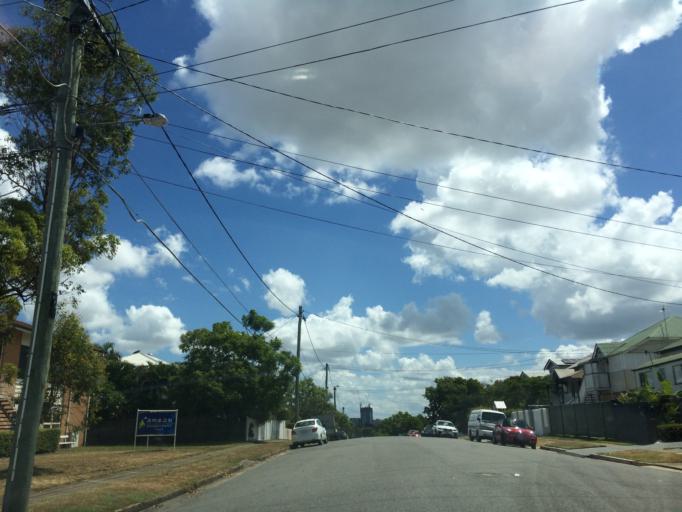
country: AU
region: Queensland
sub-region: Brisbane
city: Seven Hills
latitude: -27.4866
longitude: 153.0600
